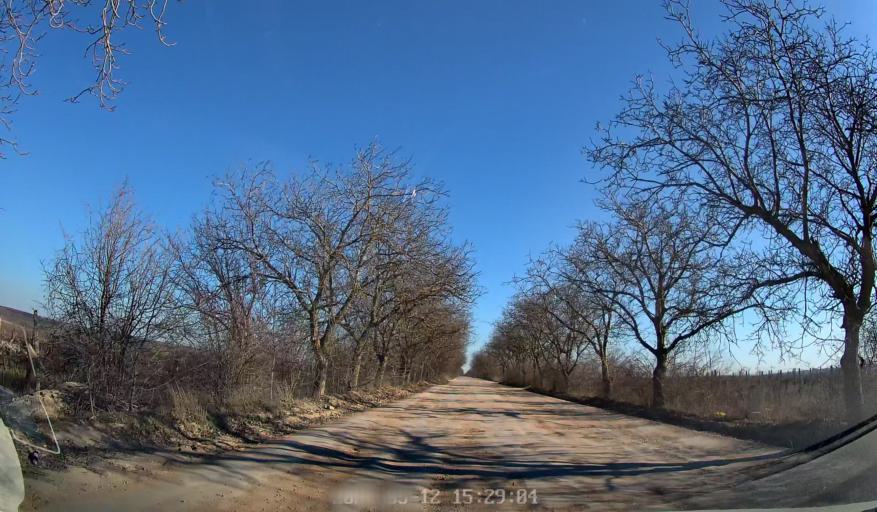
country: MD
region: Chisinau
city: Ciorescu
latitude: 47.1655
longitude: 28.9342
